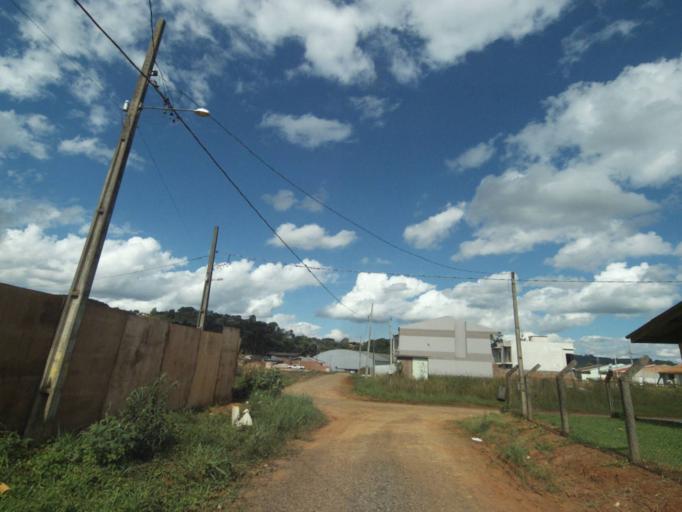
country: BR
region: Parana
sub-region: Uniao Da Vitoria
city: Uniao da Vitoria
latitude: -26.1509
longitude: -51.5420
